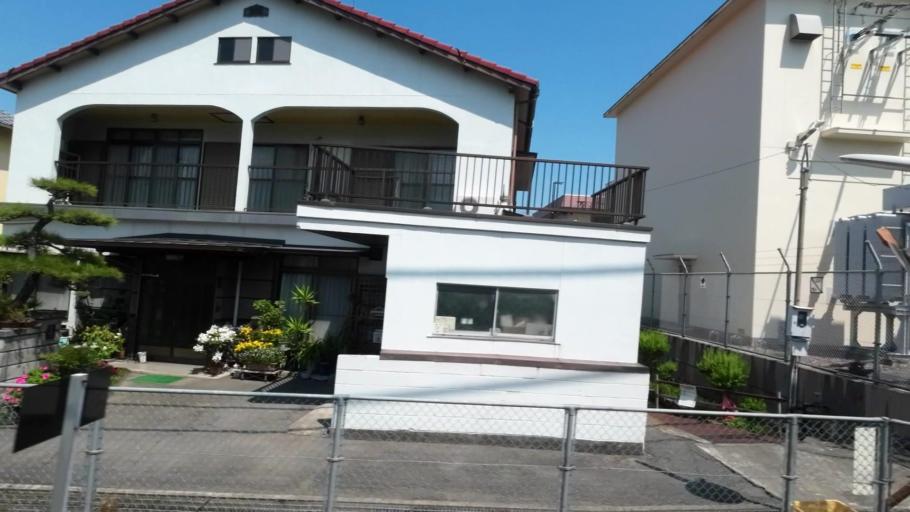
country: JP
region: Ehime
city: Saijo
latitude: 33.9116
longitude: 133.1856
